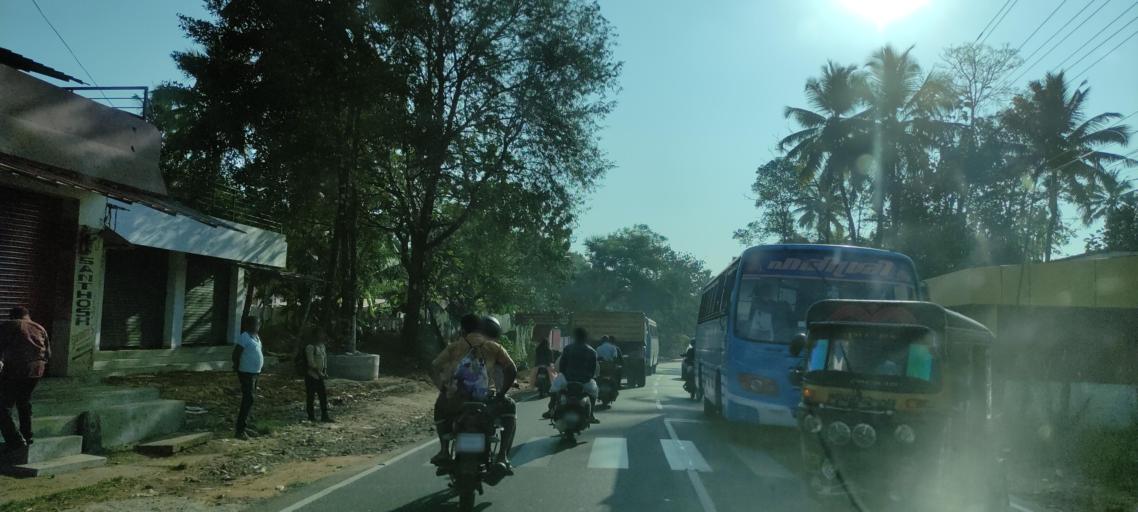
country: IN
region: Kerala
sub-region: Pattanamtitta
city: Adur
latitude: 9.1729
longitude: 76.6476
